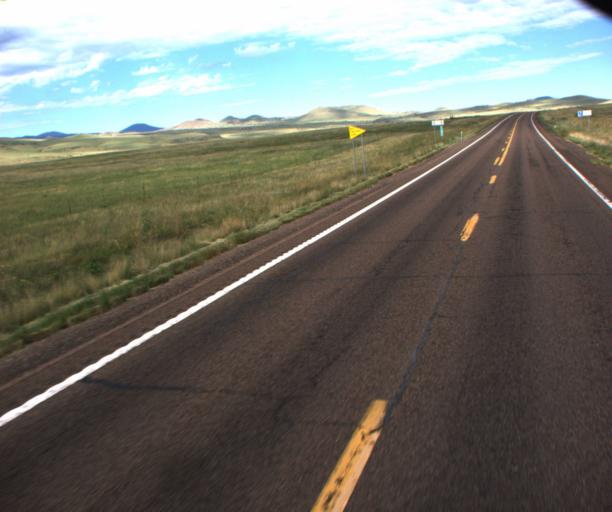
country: US
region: Arizona
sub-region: Apache County
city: Springerville
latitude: 34.1976
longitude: -109.3876
